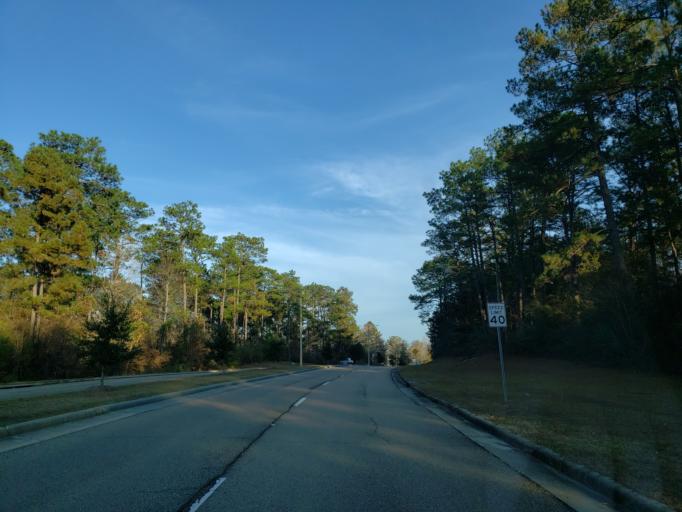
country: US
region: Mississippi
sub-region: Lamar County
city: Arnold Line
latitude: 31.3557
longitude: -89.3586
